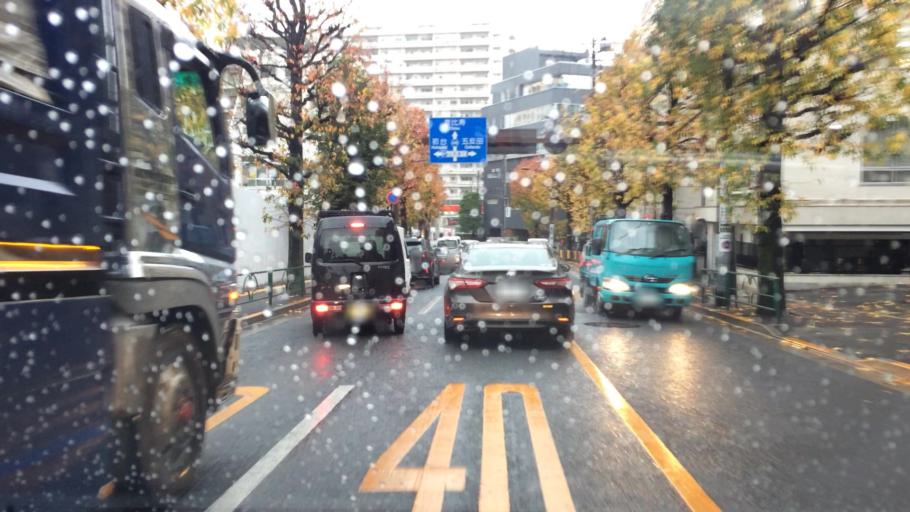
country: JP
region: Tokyo
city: Tokyo
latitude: 35.6415
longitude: 139.6997
